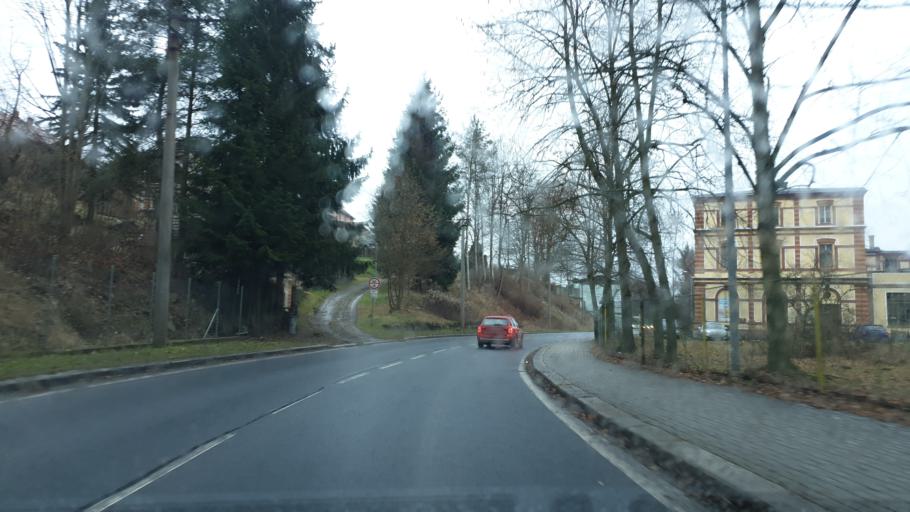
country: CZ
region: Karlovarsky
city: As
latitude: 50.2280
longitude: 12.1852
